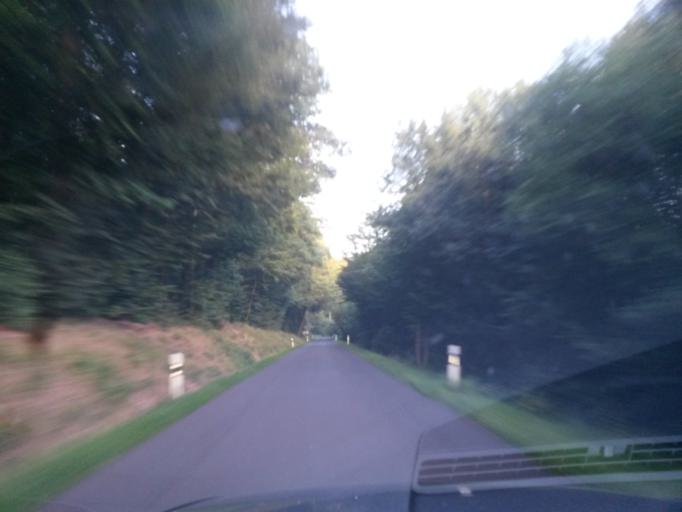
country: DE
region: Bavaria
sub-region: Regierungsbezirk Unterfranken
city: Rechtenbach
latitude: 49.9495
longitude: 9.4692
